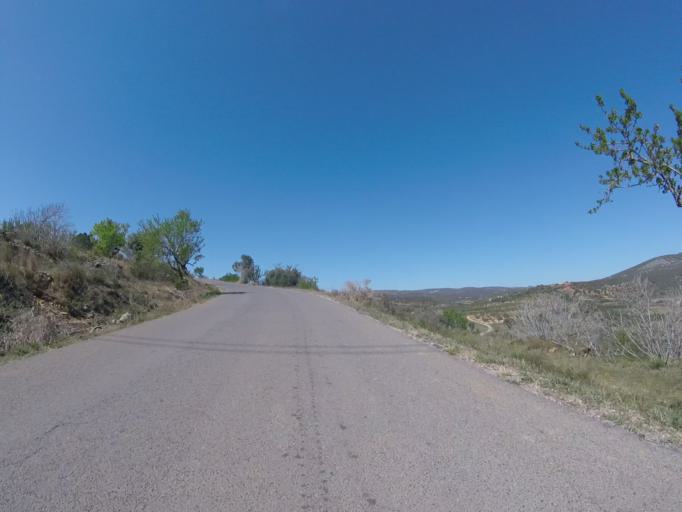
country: ES
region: Valencia
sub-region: Provincia de Castello
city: Cuevas de Vinroma
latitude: 40.3799
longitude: 0.1390
